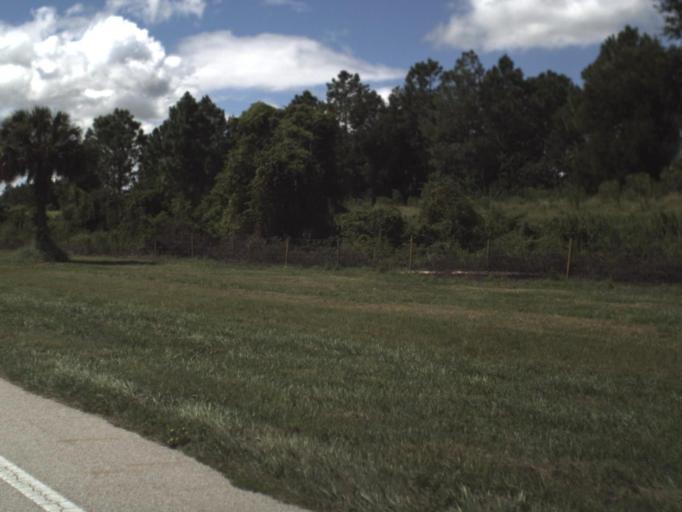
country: US
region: Florida
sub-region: Polk County
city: Mulberry
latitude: 27.8451
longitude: -81.9791
